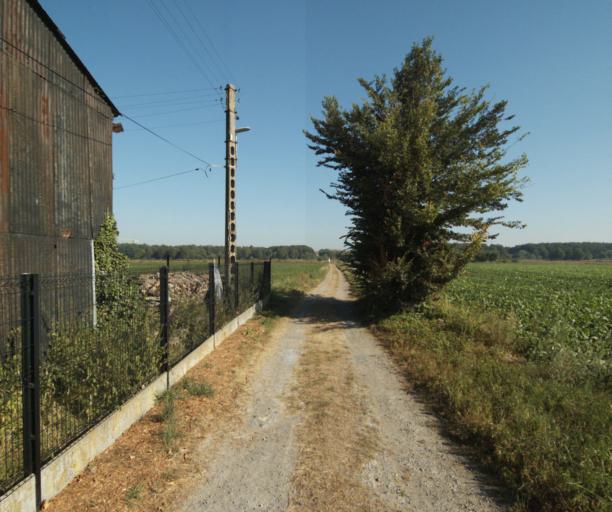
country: FR
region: Nord-Pas-de-Calais
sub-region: Departement du Nord
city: Wervicq-Sud
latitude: 50.7762
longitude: 3.0565
